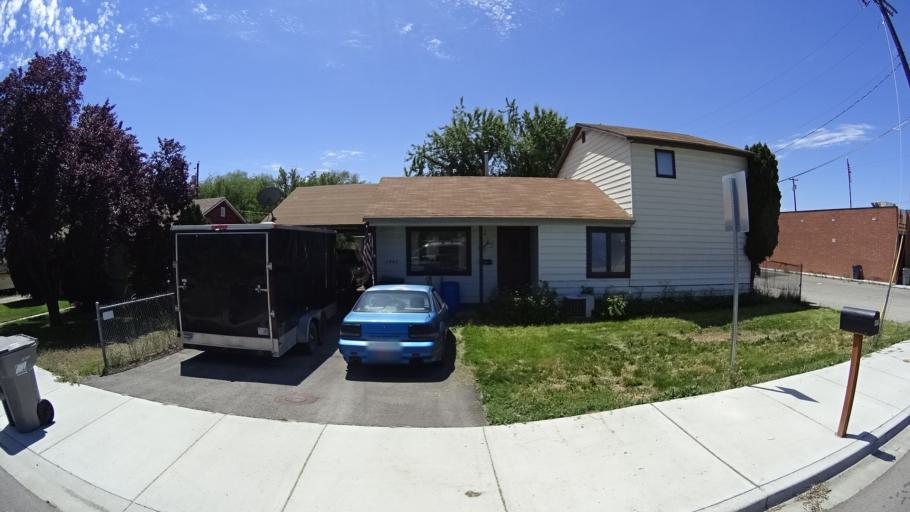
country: US
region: Idaho
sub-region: Ada County
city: Garden City
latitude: 43.6043
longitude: -116.2427
